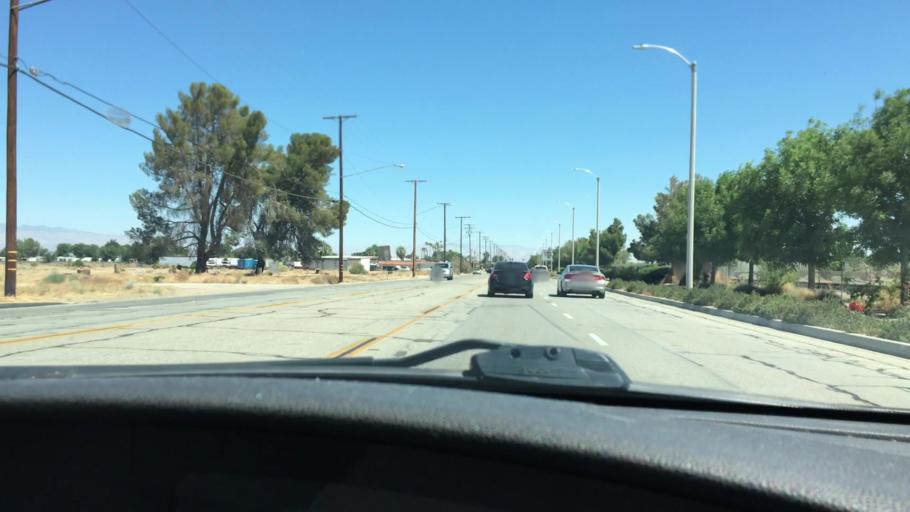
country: US
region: California
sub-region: Los Angeles County
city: Lancaster
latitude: 34.6634
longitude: -118.1310
